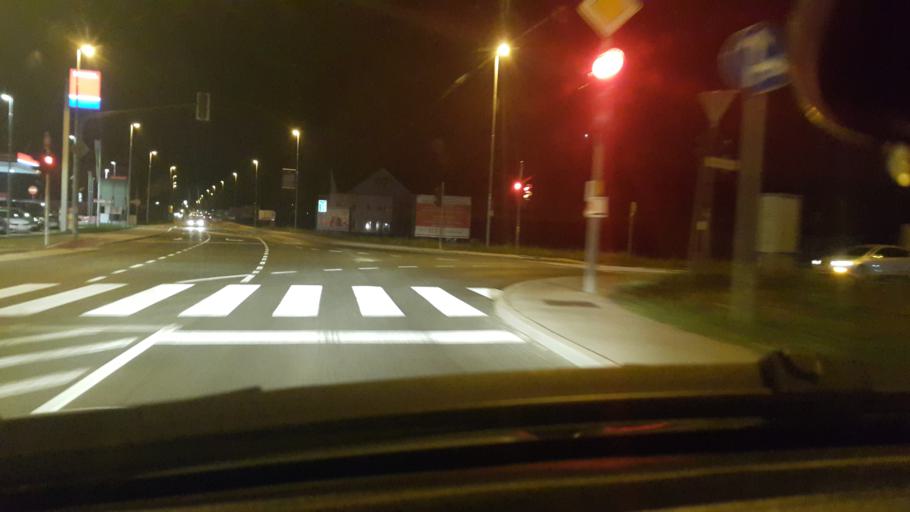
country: SI
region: Domzale
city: Domzale
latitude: 46.1355
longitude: 14.6059
